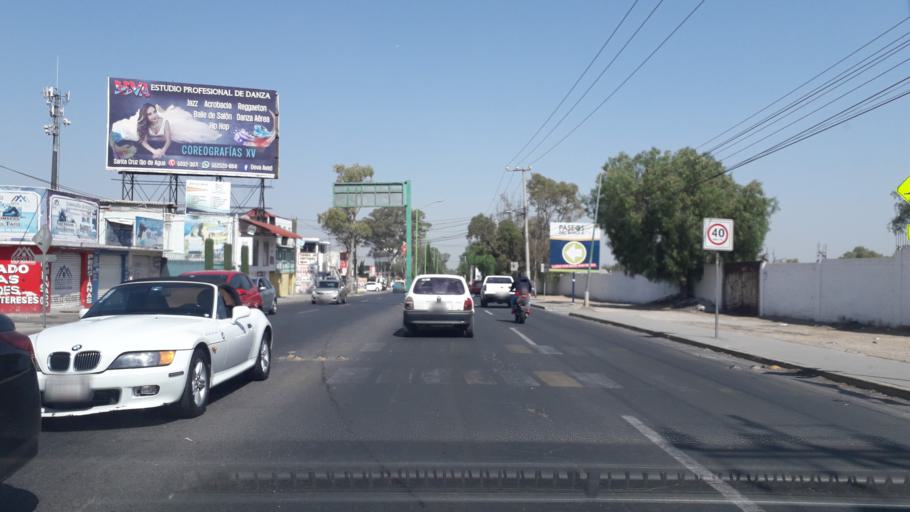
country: MX
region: Mexico
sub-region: Tecamac
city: Ojo de Agua
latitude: 19.6627
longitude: -99.0095
